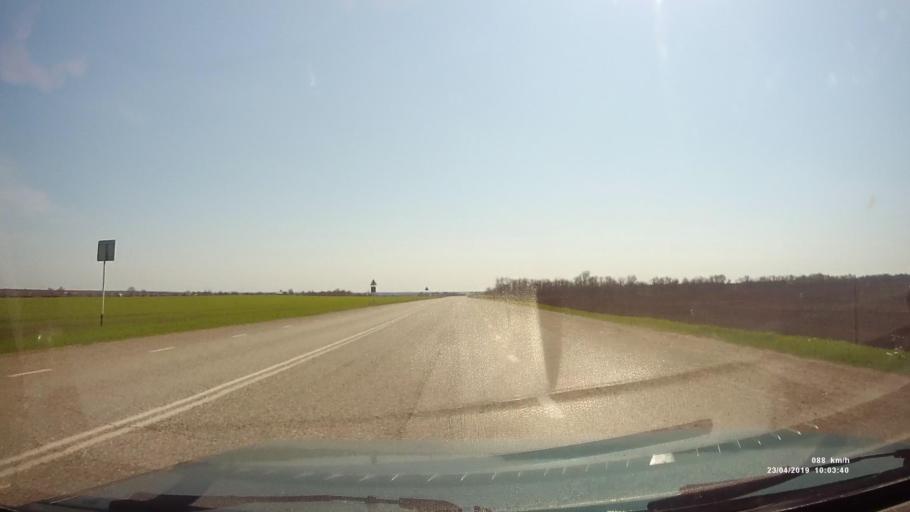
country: RU
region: Rostov
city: Sovetskoye
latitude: 46.7537
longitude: 42.1951
